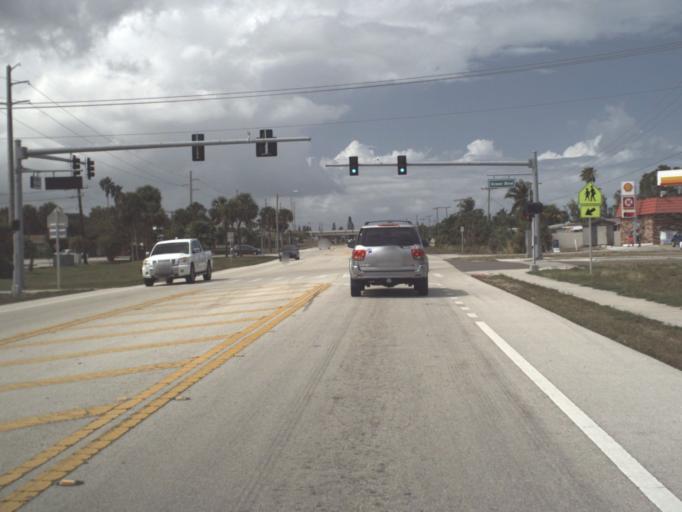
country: US
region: Florida
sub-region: Brevard County
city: South Patrick Shores
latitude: 28.2079
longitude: -80.6064
